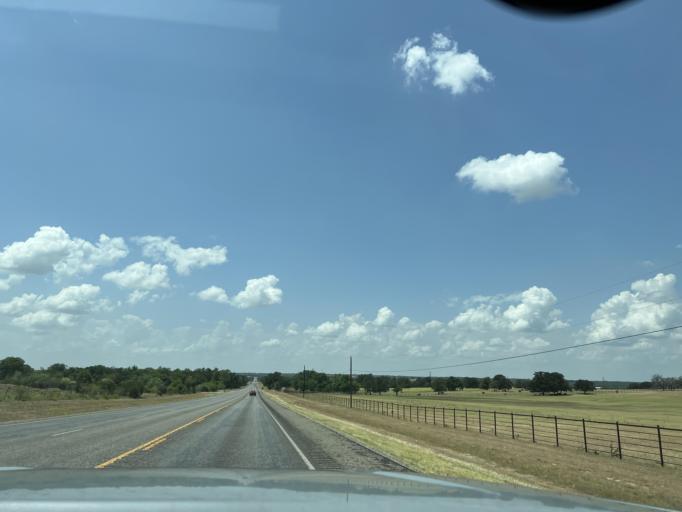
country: US
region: Texas
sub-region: Parker County
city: Springtown
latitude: 32.8905
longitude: -97.7333
